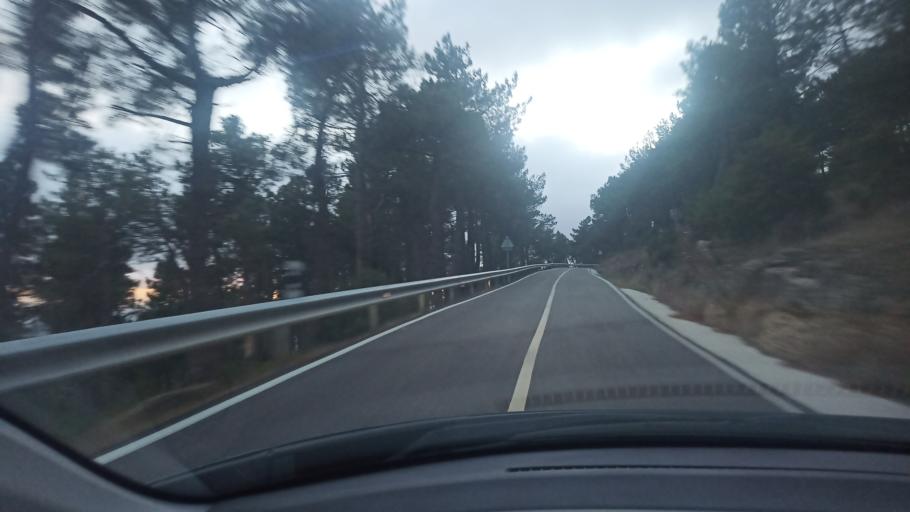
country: ES
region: Madrid
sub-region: Provincia de Madrid
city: Zarzalejo
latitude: 40.5529
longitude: -4.1930
